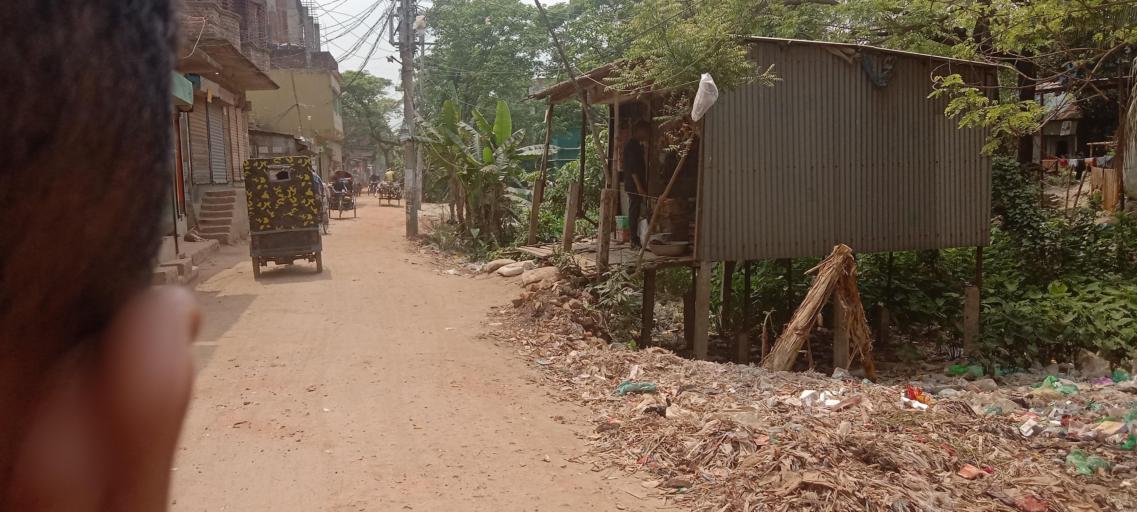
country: BD
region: Dhaka
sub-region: Dhaka
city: Dhaka
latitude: 23.6775
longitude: 90.4199
